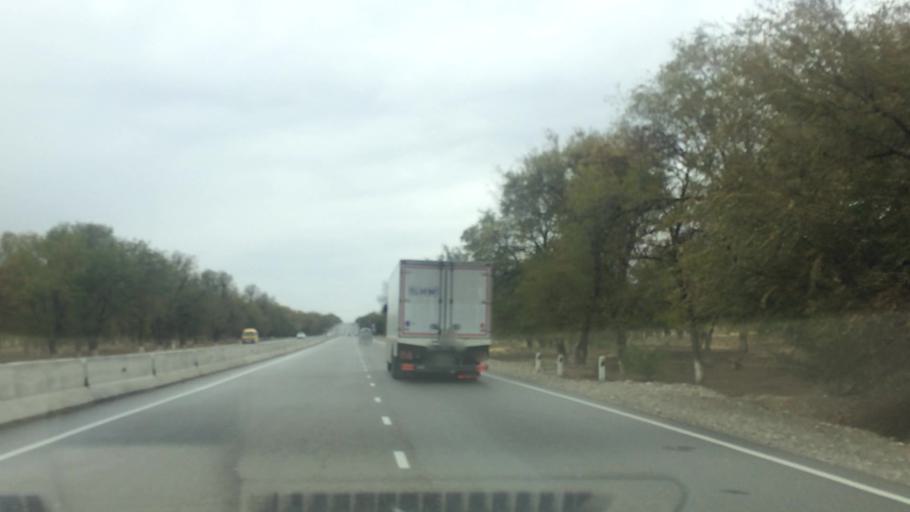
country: UZ
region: Samarqand
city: Bulung'ur
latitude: 39.8982
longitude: 67.4993
